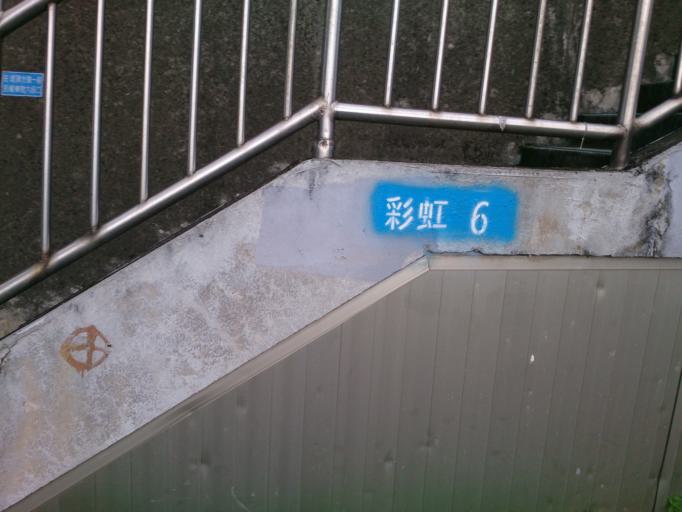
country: TW
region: Taipei
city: Taipei
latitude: 25.0657
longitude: 121.5721
